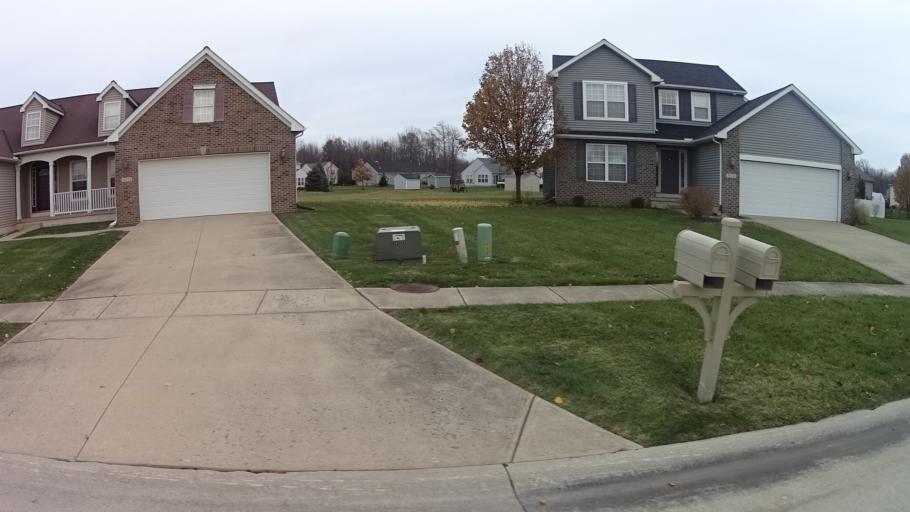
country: US
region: Ohio
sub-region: Lorain County
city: Avon
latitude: 41.4164
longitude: -82.0518
